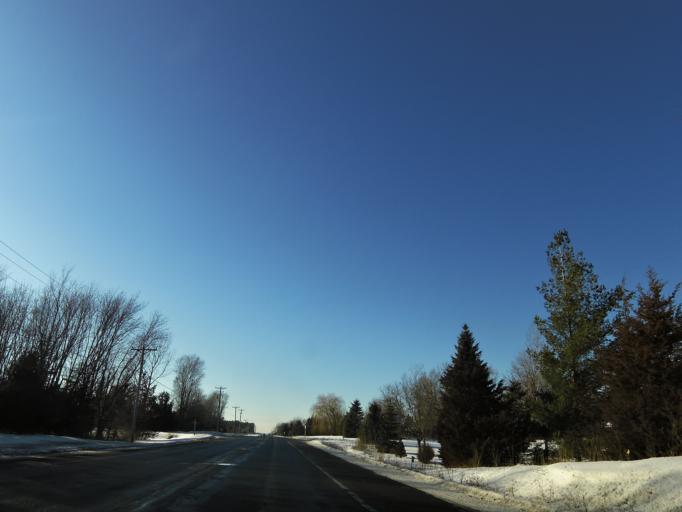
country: US
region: Wisconsin
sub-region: Saint Croix County
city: Hudson
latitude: 44.9781
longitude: -92.6878
